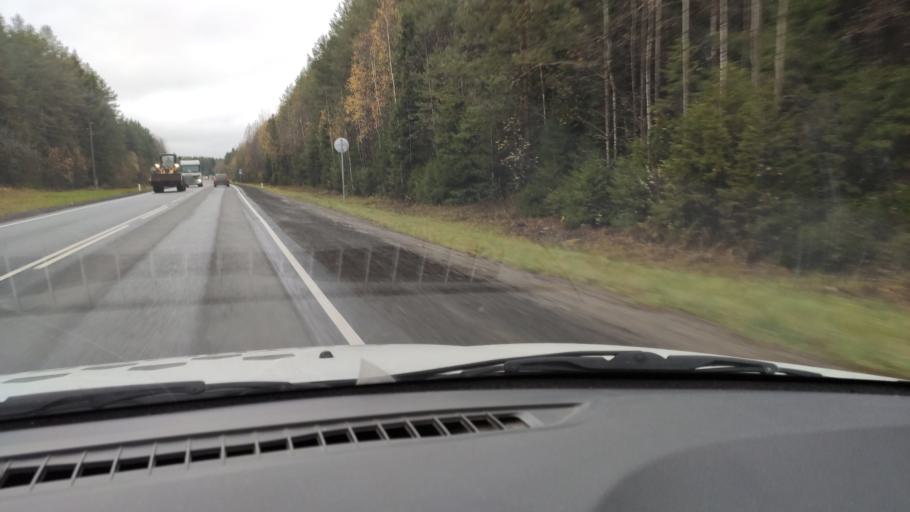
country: RU
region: Kirov
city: Belaya Kholunitsa
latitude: 58.8768
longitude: 50.8656
